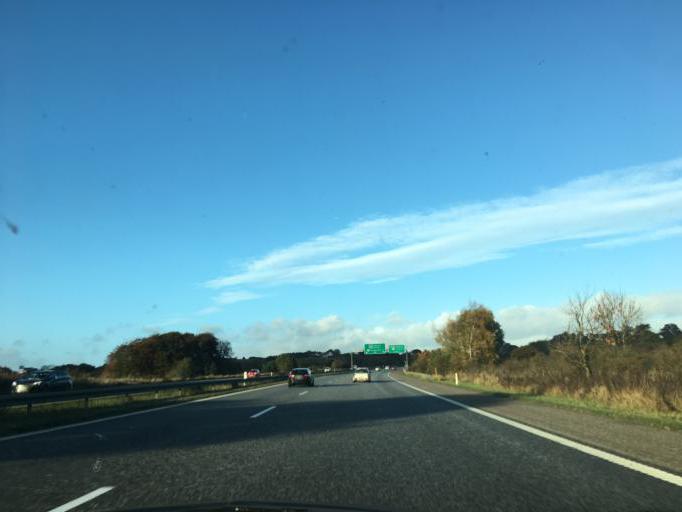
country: DK
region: South Denmark
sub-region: Kolding Kommune
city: Kolding
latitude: 55.5001
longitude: 9.4209
